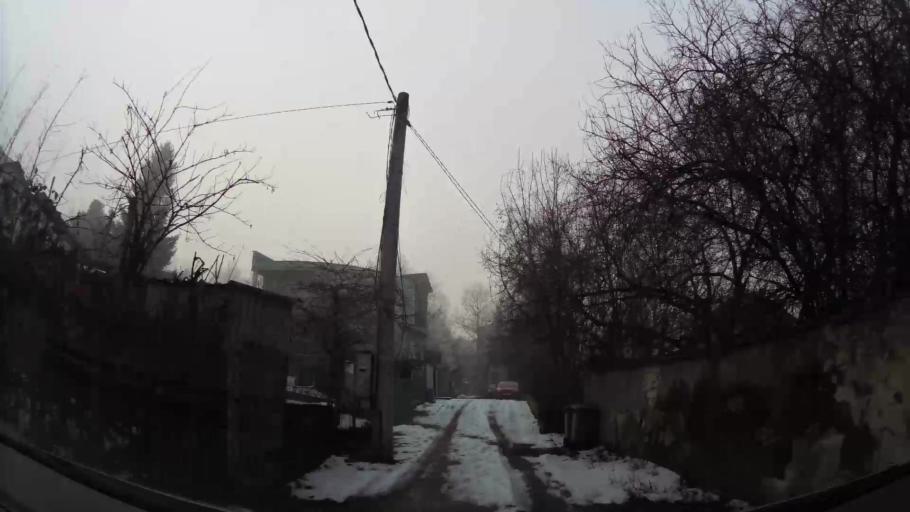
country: BG
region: Sofia-Capital
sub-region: Stolichna Obshtina
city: Sofia
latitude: 42.6595
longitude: 23.2469
